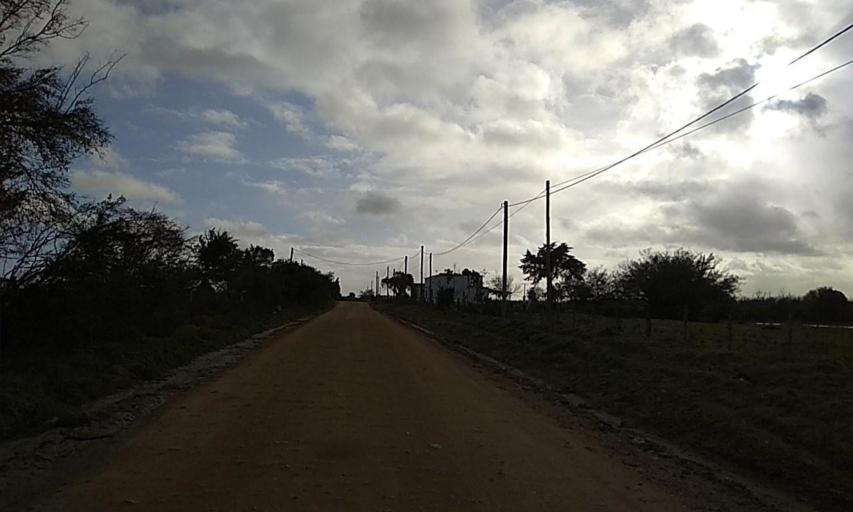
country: UY
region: Florida
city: Florida
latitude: -34.0615
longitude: -56.1925
